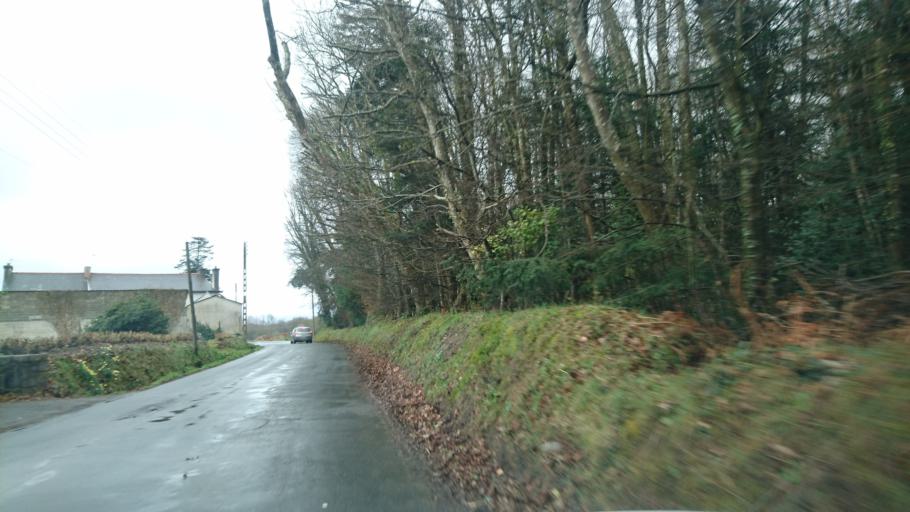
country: FR
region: Brittany
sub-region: Departement des Cotes-d'Armor
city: Louannec
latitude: 48.7783
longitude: -3.4144
